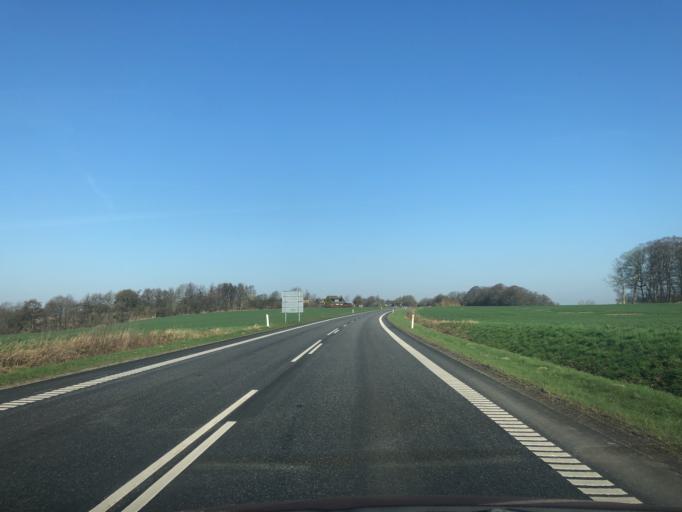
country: DK
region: Zealand
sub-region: Faxe Kommune
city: Ronnede
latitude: 55.2901
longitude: 12.0127
